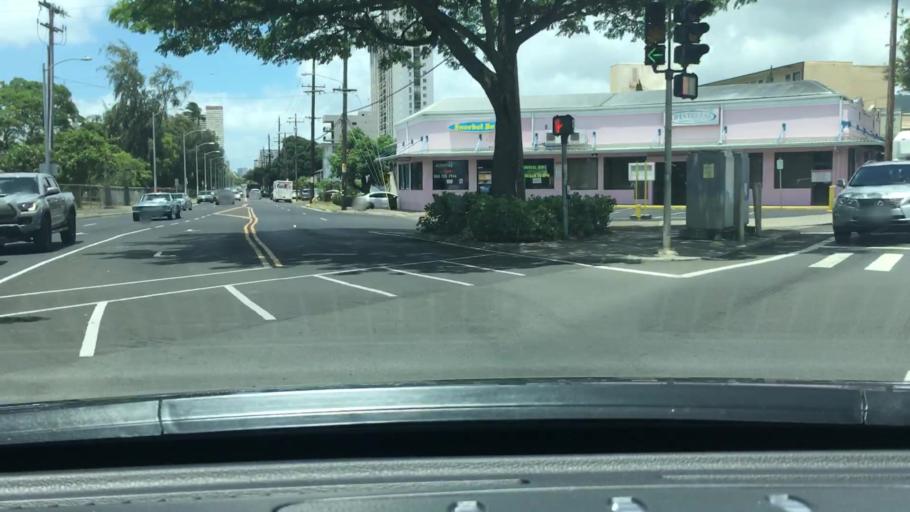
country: US
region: Hawaii
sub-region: Honolulu County
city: Honolulu
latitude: 21.2793
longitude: -157.8140
